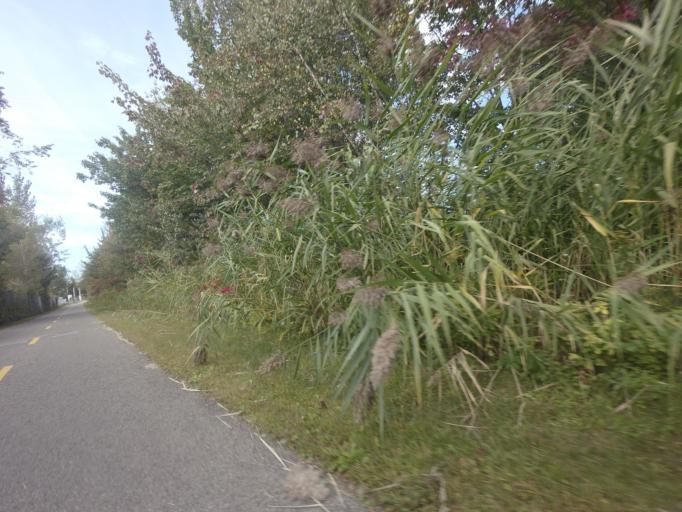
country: CA
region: Quebec
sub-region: Laurentides
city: Blainville
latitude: 45.6974
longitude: -73.8992
